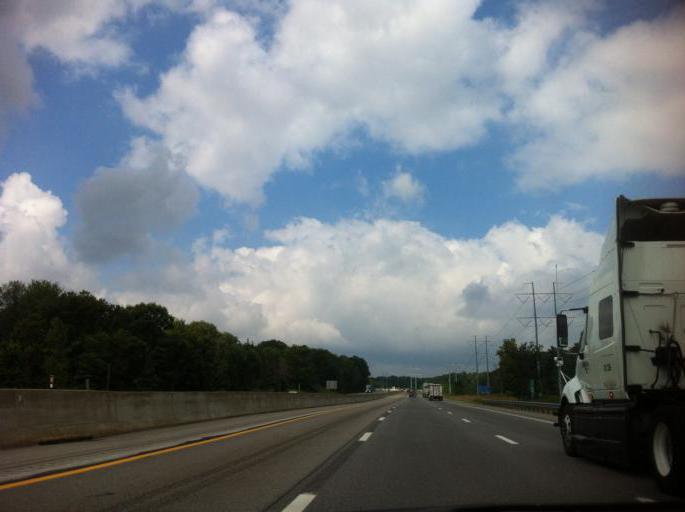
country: US
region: Ohio
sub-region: Cuyahoga County
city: Broadview Heights
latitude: 41.2981
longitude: -81.6933
